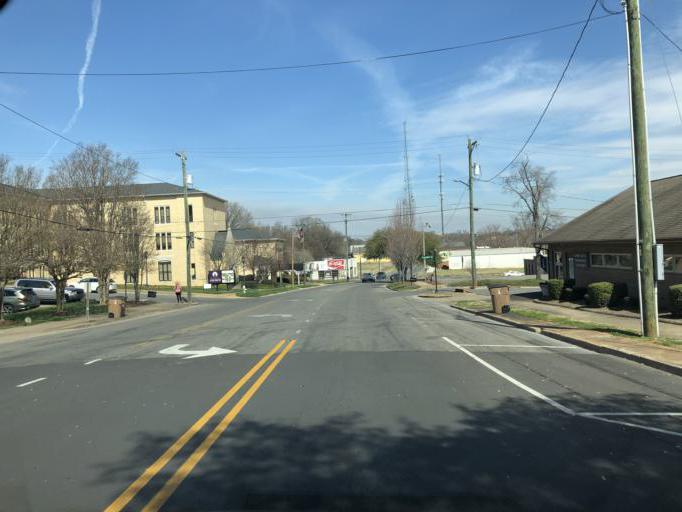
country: US
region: North Carolina
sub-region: Cleveland County
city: Shelby
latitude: 35.2921
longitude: -81.5389
